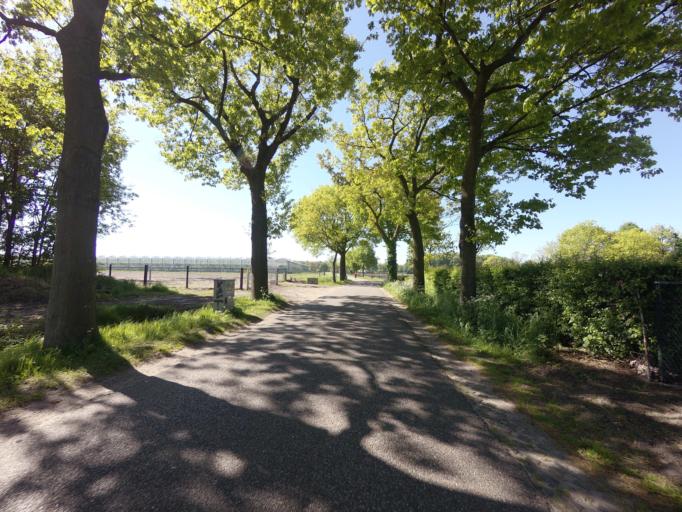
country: NL
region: North Brabant
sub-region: Gemeente Rucphen
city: Rucphen
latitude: 51.5817
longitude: 4.5579
